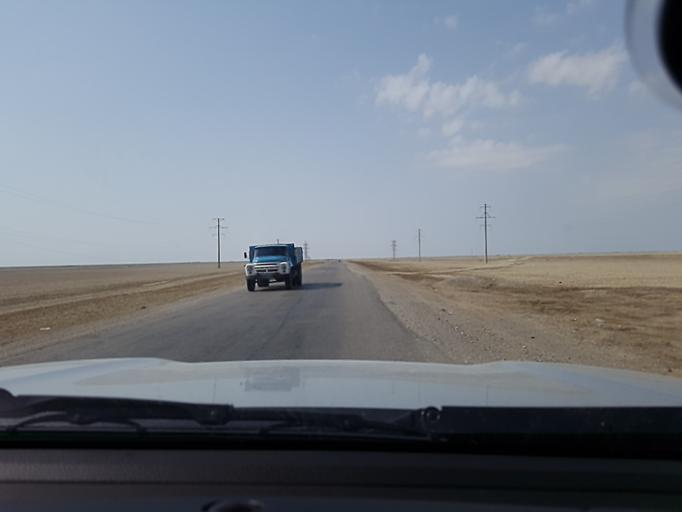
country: TM
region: Balkan
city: Gumdag
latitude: 39.0586
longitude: 54.5842
